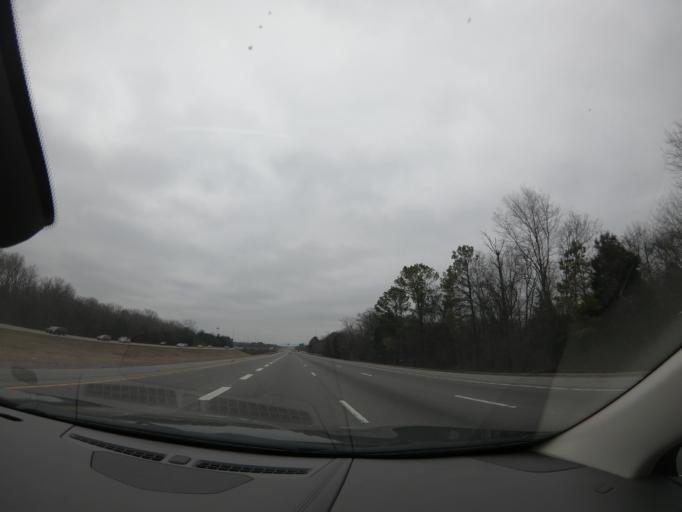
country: US
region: Tennessee
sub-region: Rutherford County
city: Smyrna
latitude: 35.9302
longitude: -86.5267
